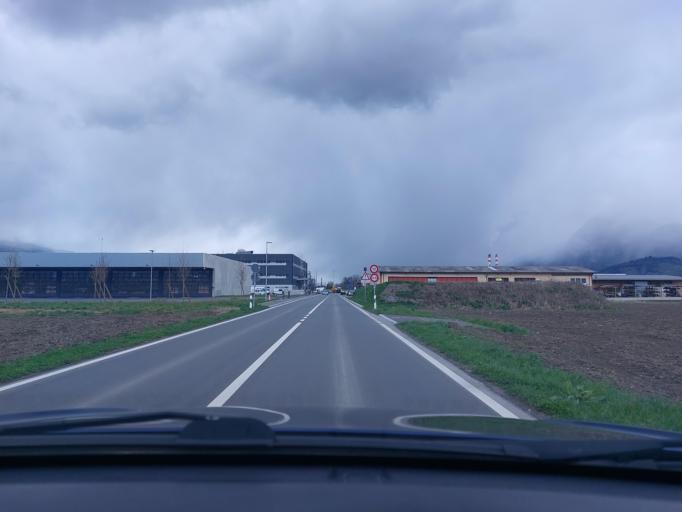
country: CH
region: Valais
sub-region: Monthey District
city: Collombey
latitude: 46.2675
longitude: 6.9594
